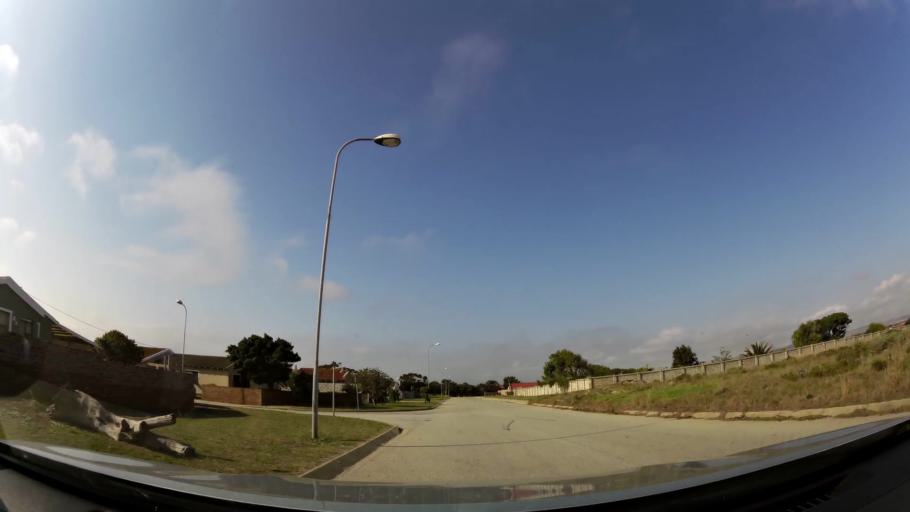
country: ZA
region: Eastern Cape
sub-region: Nelson Mandela Bay Metropolitan Municipality
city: Port Elizabeth
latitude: -33.9193
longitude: 25.5327
